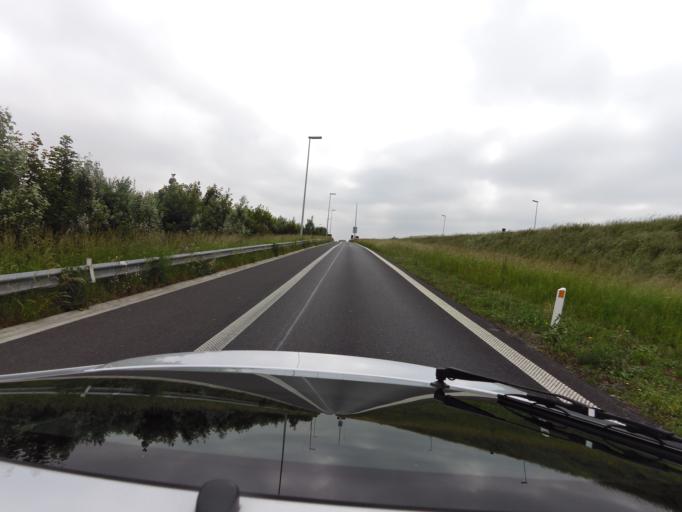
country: BE
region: Flanders
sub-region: Provincie West-Vlaanderen
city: Veurne
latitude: 51.0570
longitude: 2.6685
